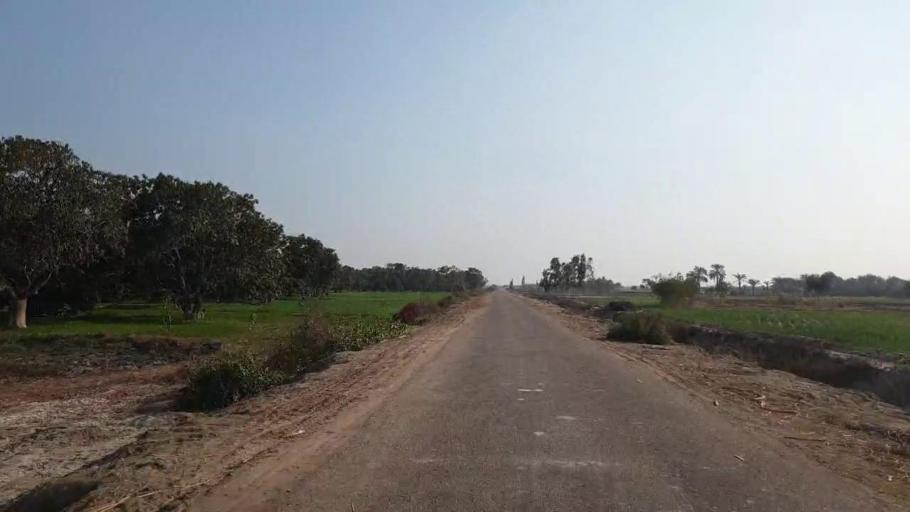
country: PK
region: Sindh
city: Tando Allahyar
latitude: 25.5968
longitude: 68.6180
